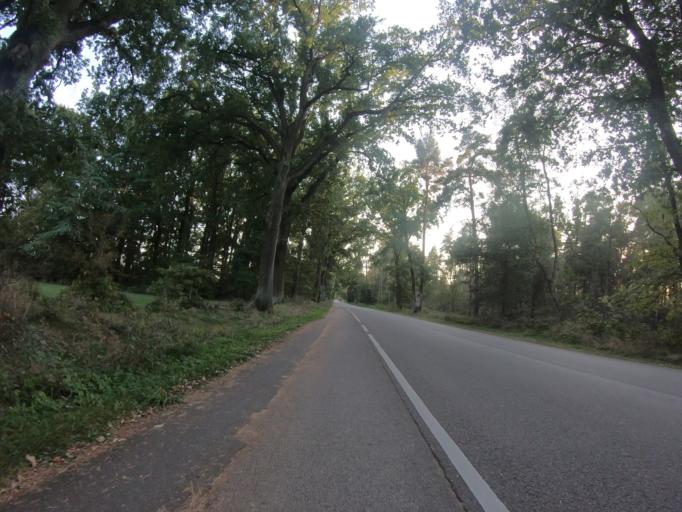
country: DE
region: Lower Saxony
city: Calberlah
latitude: 52.4480
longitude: 10.6114
